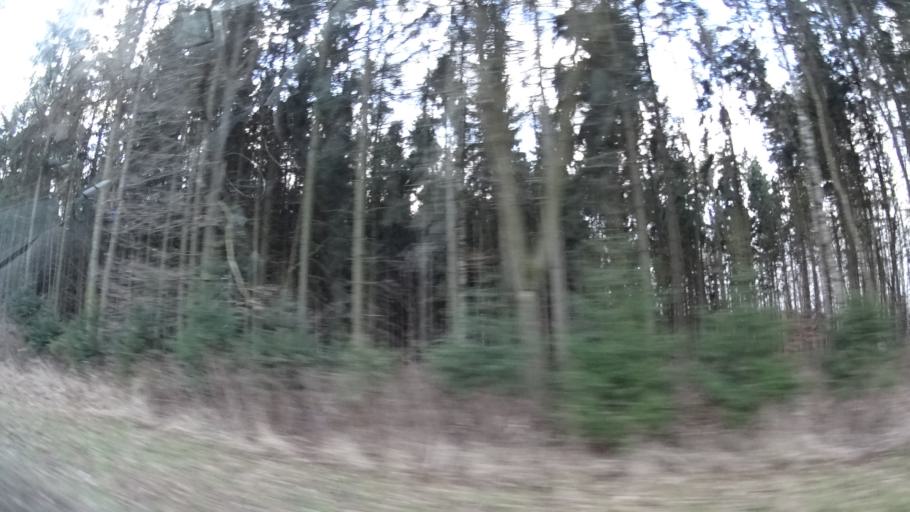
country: DE
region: Thuringia
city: Auma
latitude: 50.6766
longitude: 11.9319
